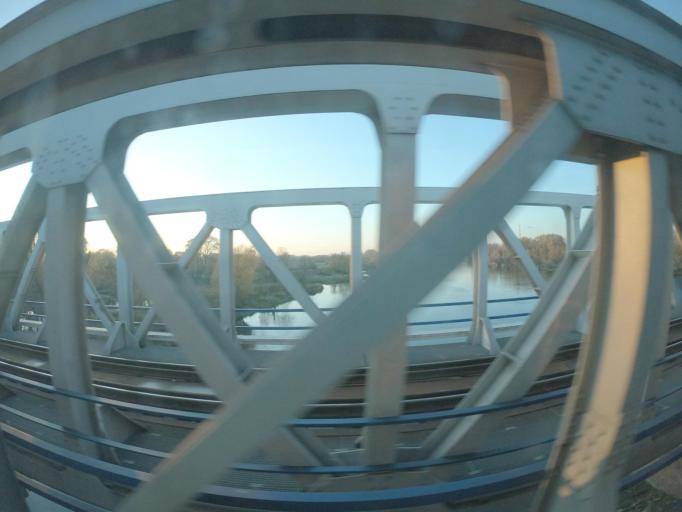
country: PL
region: Lubusz
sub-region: Powiat gorzowski
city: Kostrzyn nad Odra
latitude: 52.5841
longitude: 14.6433
